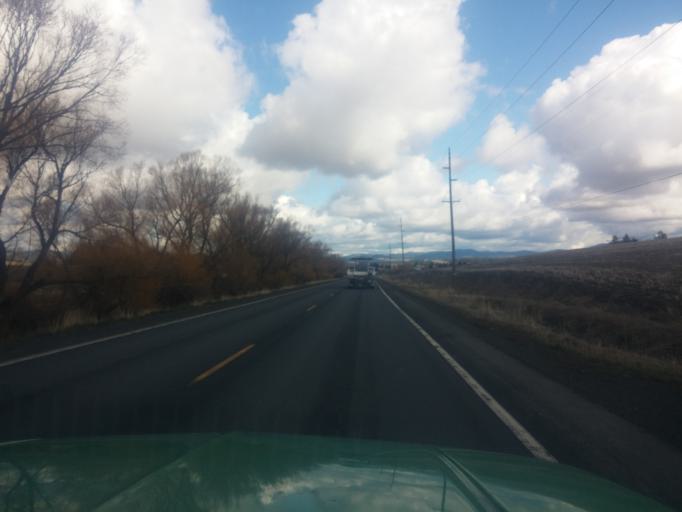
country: US
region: Idaho
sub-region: Latah County
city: Moscow
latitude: 46.8935
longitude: -116.9930
